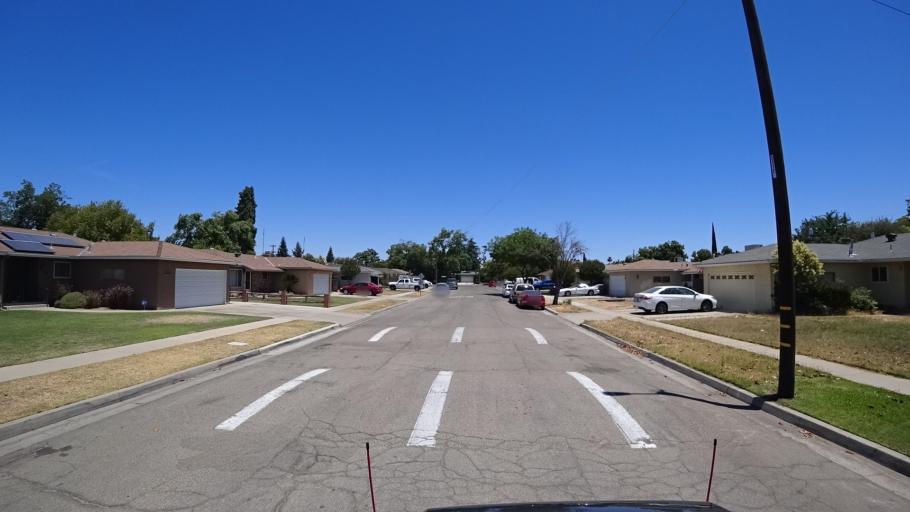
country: US
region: California
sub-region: Fresno County
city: Tarpey Village
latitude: 36.7996
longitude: -119.7510
